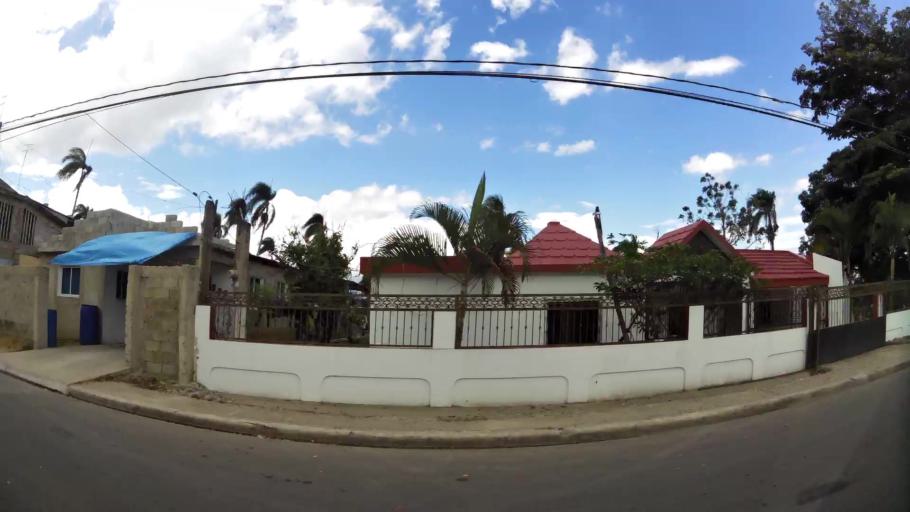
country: DO
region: Santiago
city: Licey al Medio
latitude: 19.3937
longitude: -70.6437
